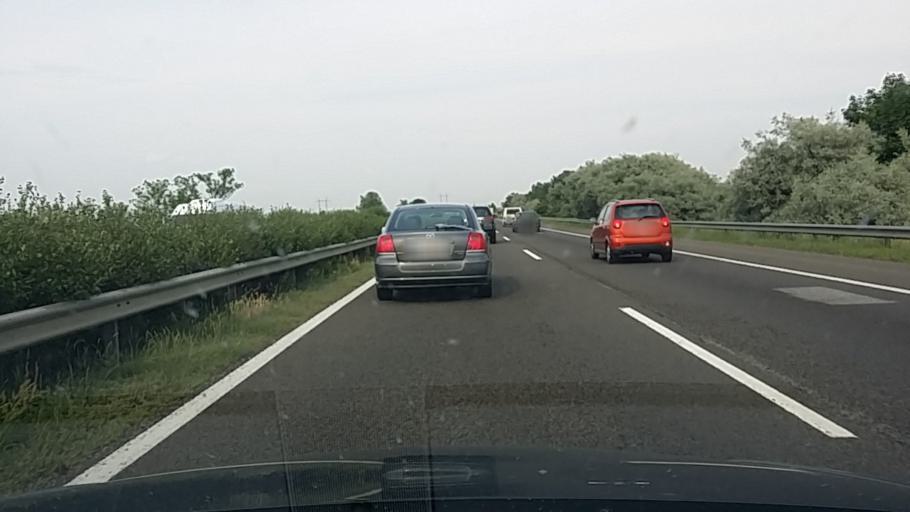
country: HU
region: Pest
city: Kartal
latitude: 47.6504
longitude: 19.5547
